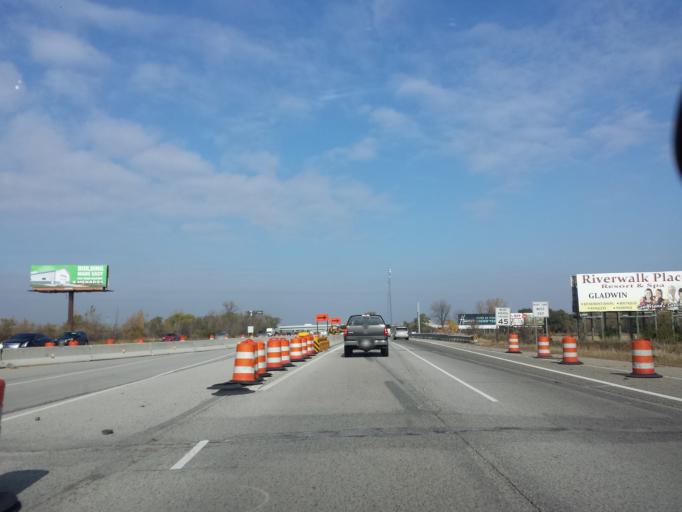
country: US
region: Michigan
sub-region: Saginaw County
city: Buena Vista
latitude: 43.4251
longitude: -83.8906
